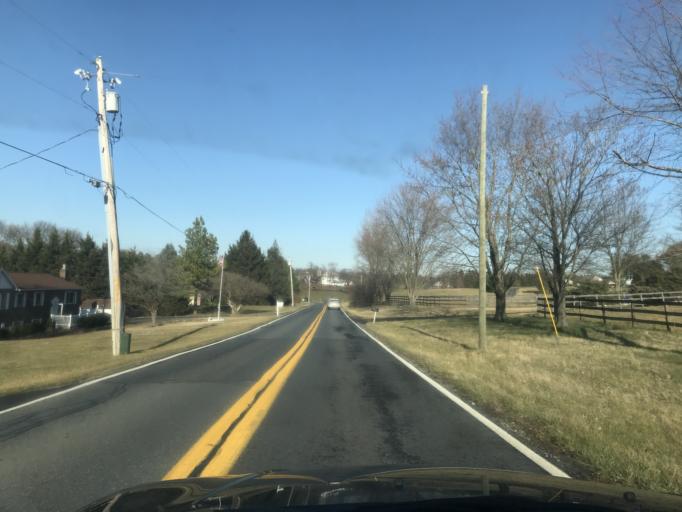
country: US
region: Maryland
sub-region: Montgomery County
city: Damascus
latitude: 39.3241
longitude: -77.2293
